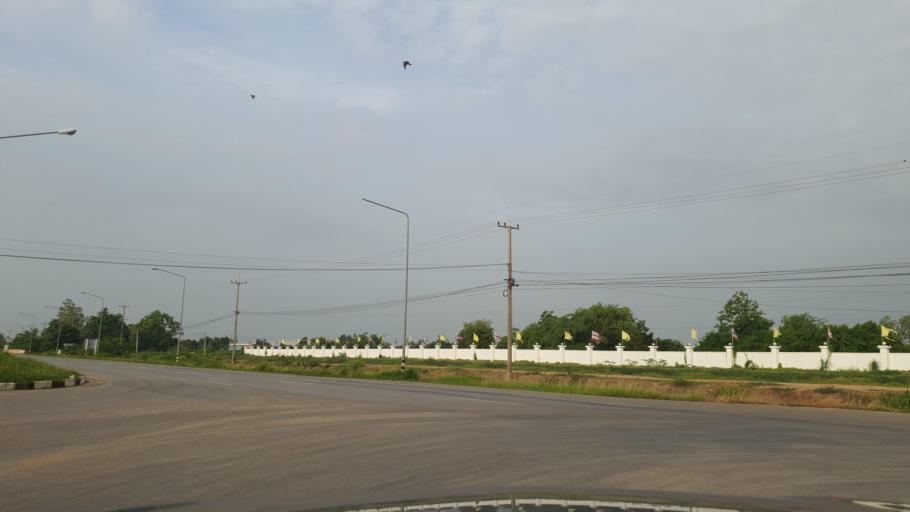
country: TH
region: Phitsanulok
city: Phitsanulok
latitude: 16.8030
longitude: 100.3316
